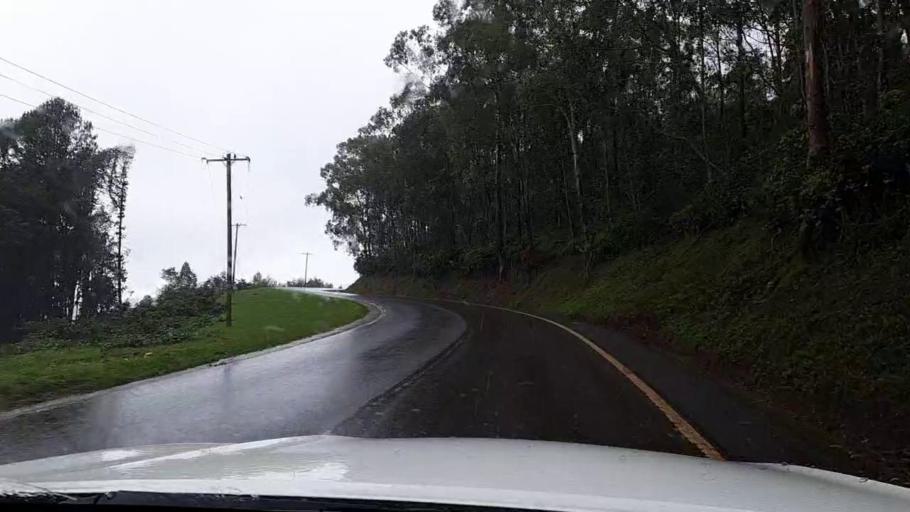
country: RW
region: Western Province
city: Cyangugu
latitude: -2.4624
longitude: 28.9942
